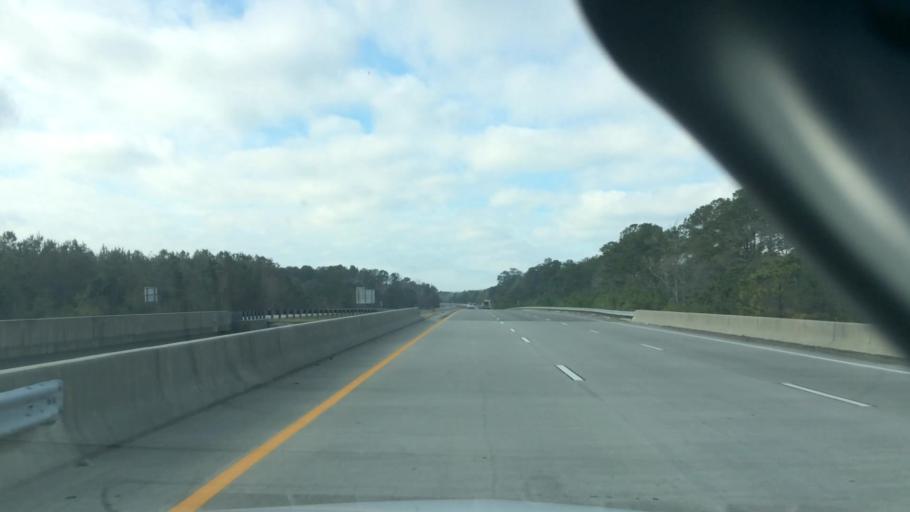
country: US
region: North Carolina
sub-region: New Hanover County
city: Wrightsboro
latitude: 34.3172
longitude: -77.9221
